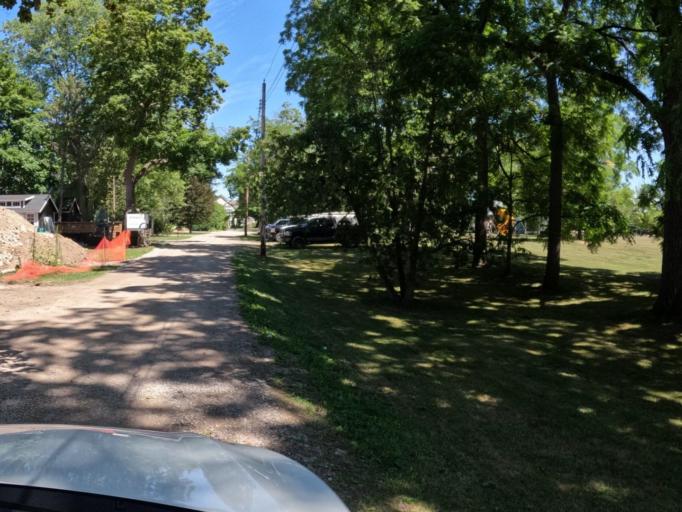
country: CA
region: Ontario
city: Cambridge
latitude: 43.4131
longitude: -80.2668
